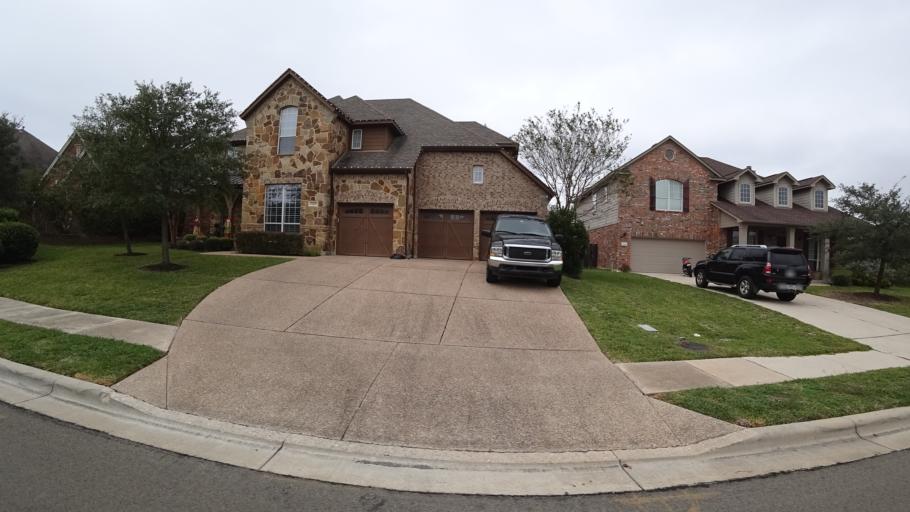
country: US
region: Texas
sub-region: Travis County
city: Barton Creek
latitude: 30.2398
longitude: -97.9040
